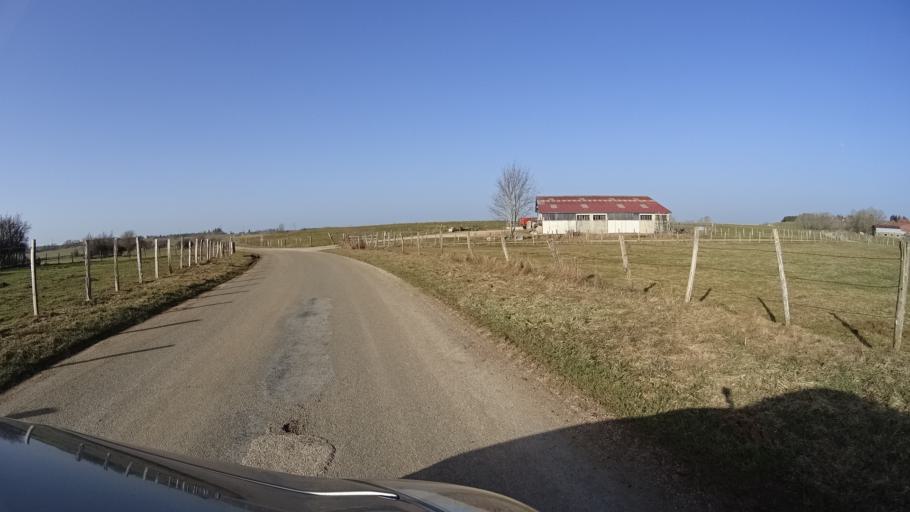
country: FR
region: Franche-Comte
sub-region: Departement du Doubs
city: Frasne
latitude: 46.8939
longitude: 6.2165
